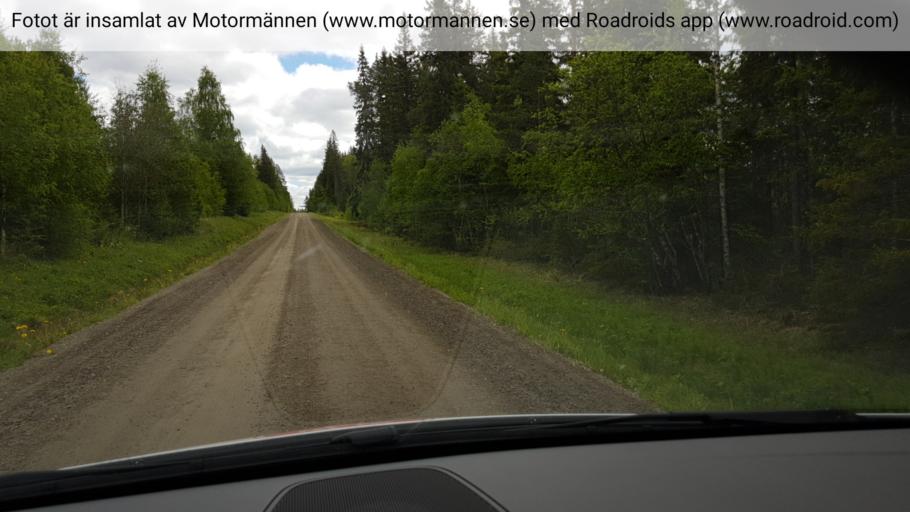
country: SE
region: Jaemtland
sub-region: Braecke Kommun
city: Braecke
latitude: 62.8003
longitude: 15.2433
